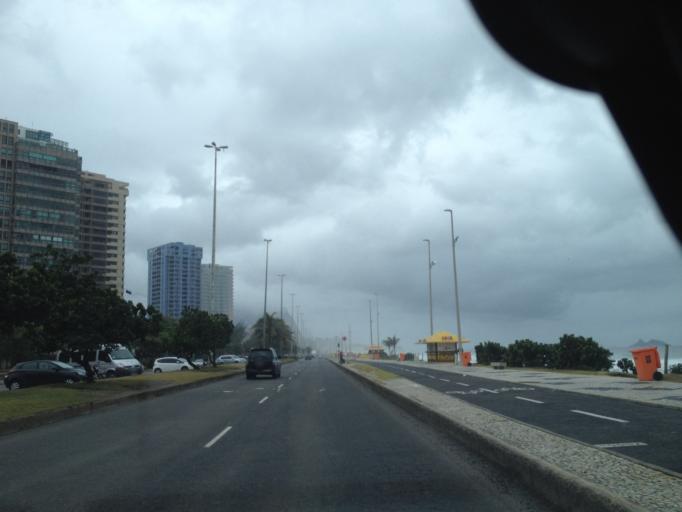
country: BR
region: Rio de Janeiro
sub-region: Rio De Janeiro
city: Rio de Janeiro
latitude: -23.0110
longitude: -43.3694
